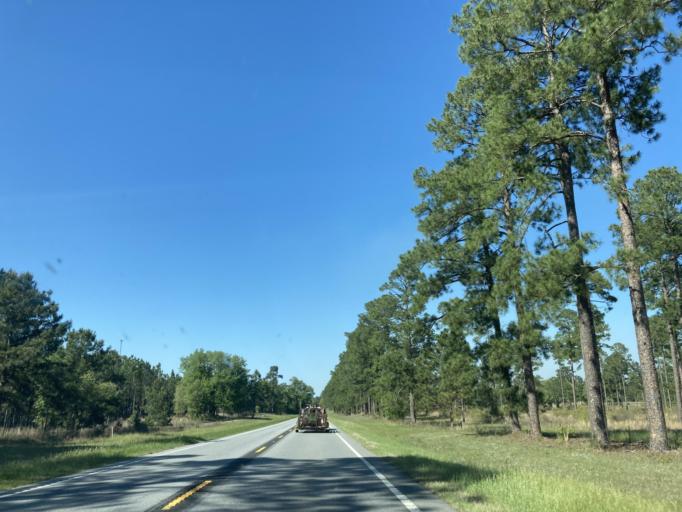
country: US
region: Georgia
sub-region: Baker County
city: Newton
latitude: 31.3815
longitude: -84.2823
